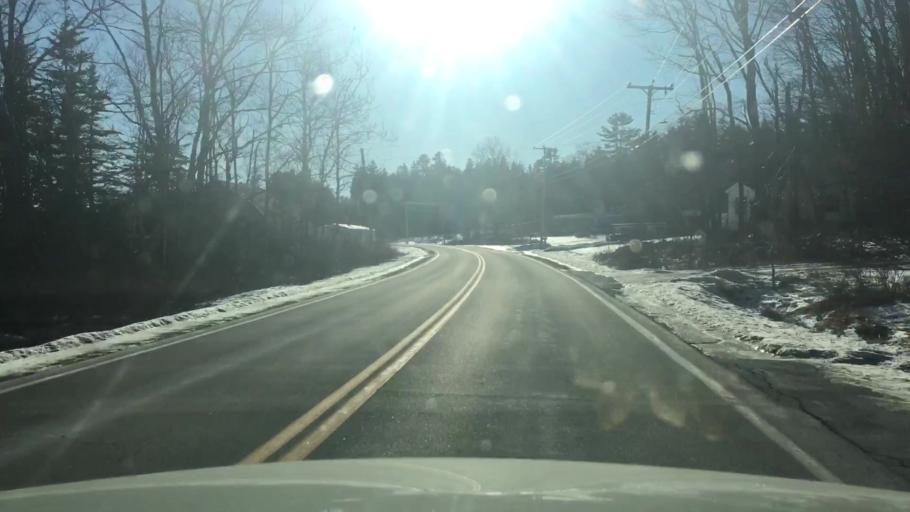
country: US
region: Maine
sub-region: Hancock County
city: Orland
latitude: 44.5204
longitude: -68.7489
